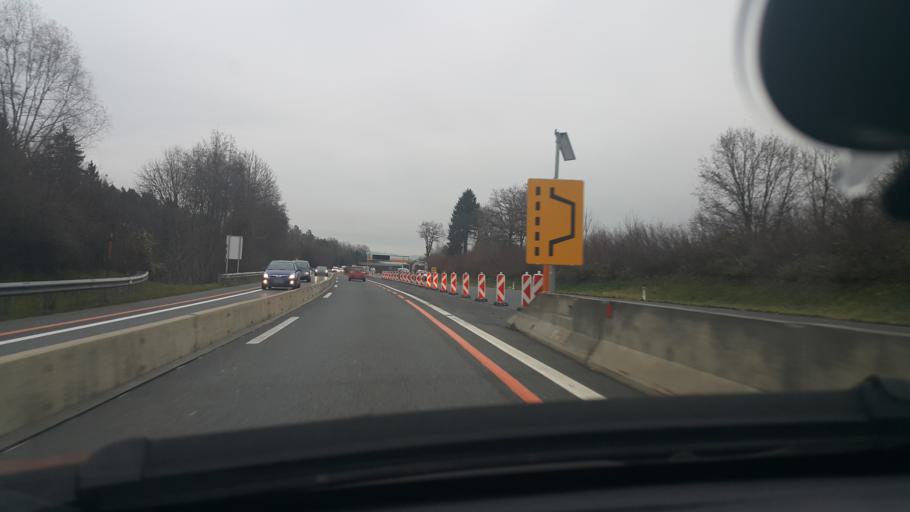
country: AT
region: Carinthia
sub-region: Klagenfurt am Woerthersee
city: Klagenfurt am Woerthersee
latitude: 46.6506
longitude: 14.2625
